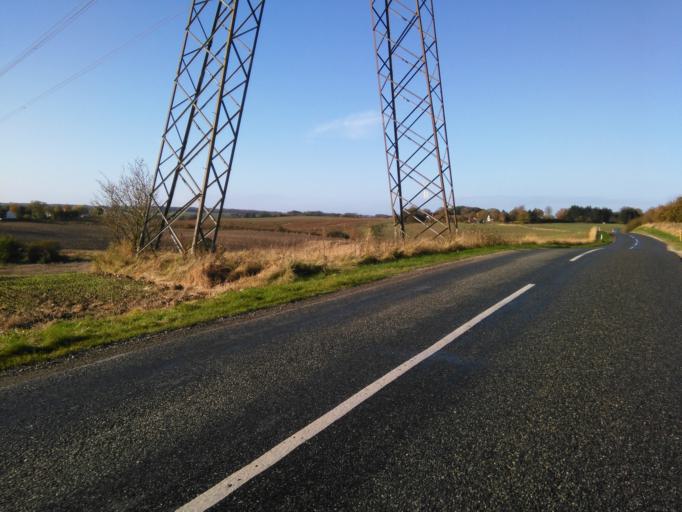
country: DK
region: Central Jutland
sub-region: Arhus Kommune
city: Marslet
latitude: 56.0322
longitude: 10.1357
